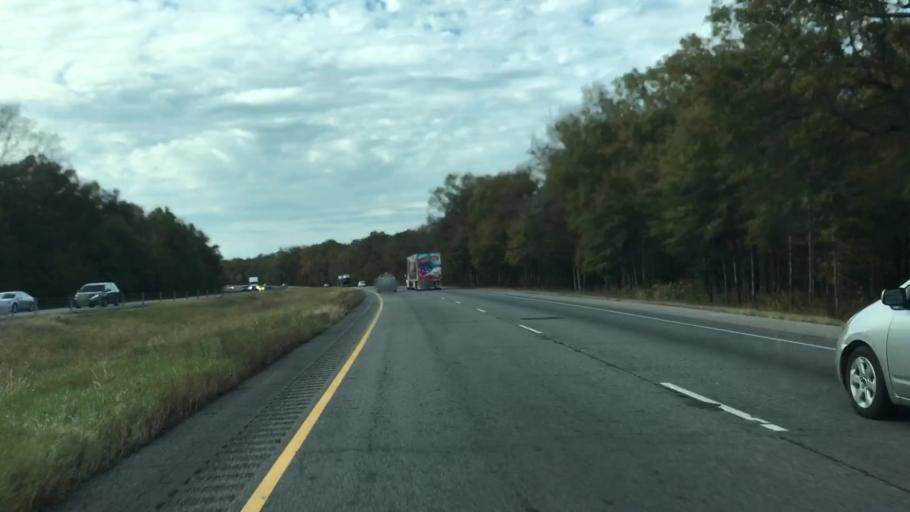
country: US
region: Arkansas
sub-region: Pope County
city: Atkins
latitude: 35.2440
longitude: -92.8629
